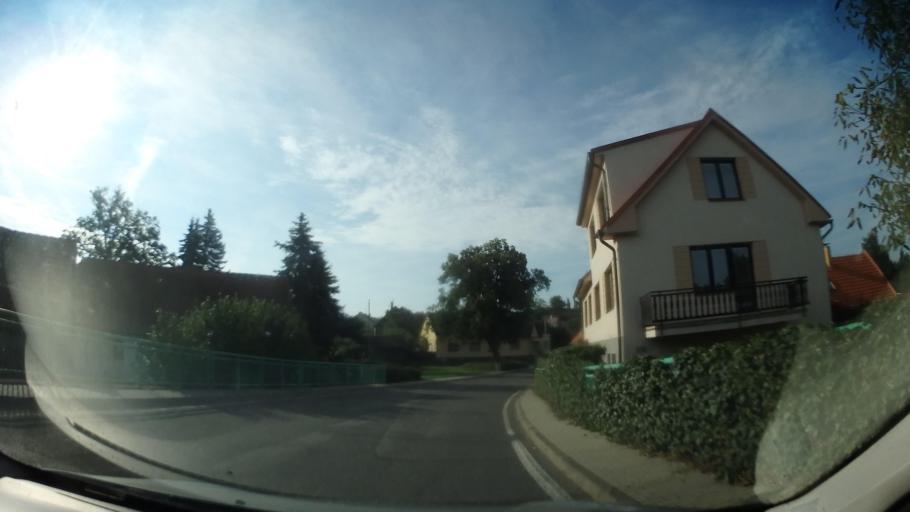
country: CZ
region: Jihocesky
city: Cimelice
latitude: 49.4193
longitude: 14.1170
